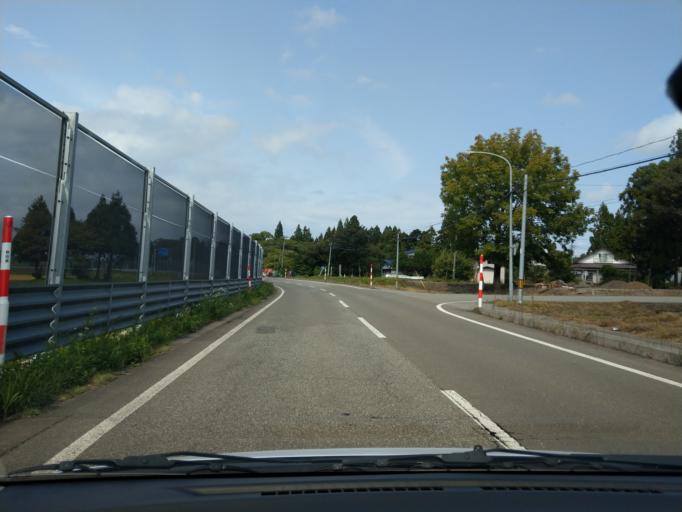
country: JP
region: Akita
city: Omagari
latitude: 39.5274
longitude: 140.2631
